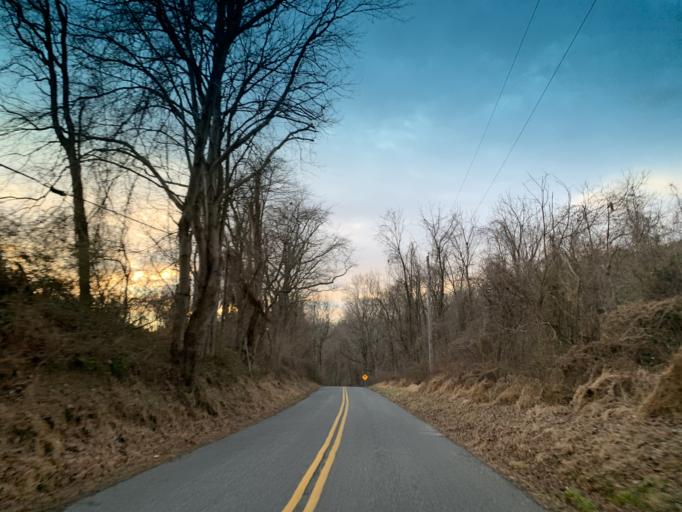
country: US
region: Maryland
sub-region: Harford County
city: Bel Air North
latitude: 39.6282
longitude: -76.3073
